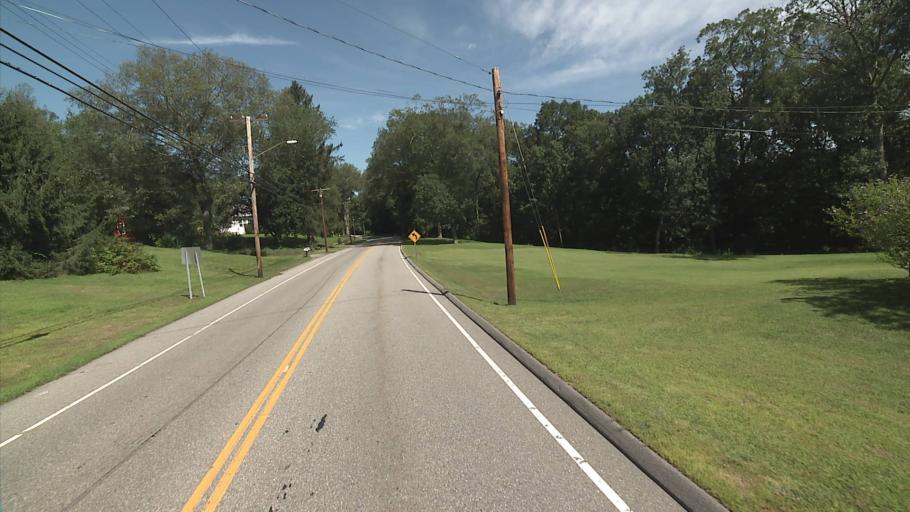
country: US
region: Connecticut
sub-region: New London County
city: Baltic
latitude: 41.6018
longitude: -72.0560
